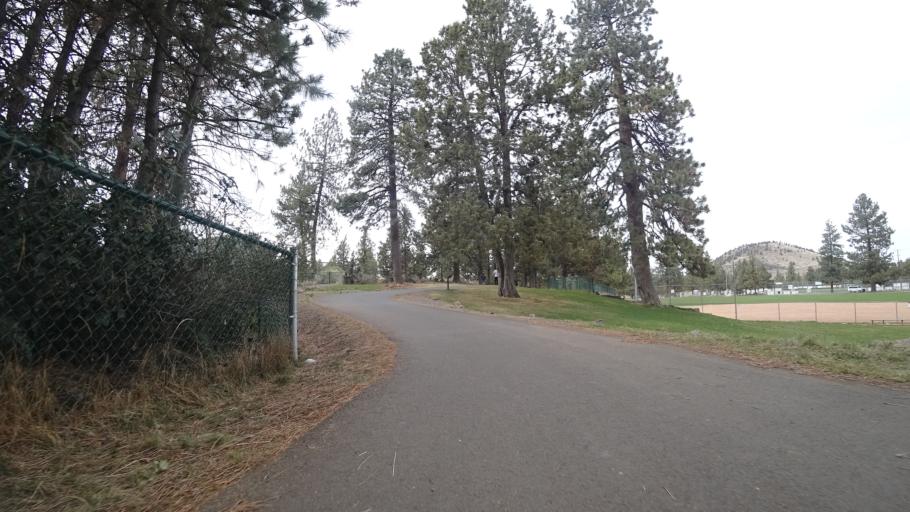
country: US
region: Oregon
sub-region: Deschutes County
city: Bend
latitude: 44.0465
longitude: -121.2849
